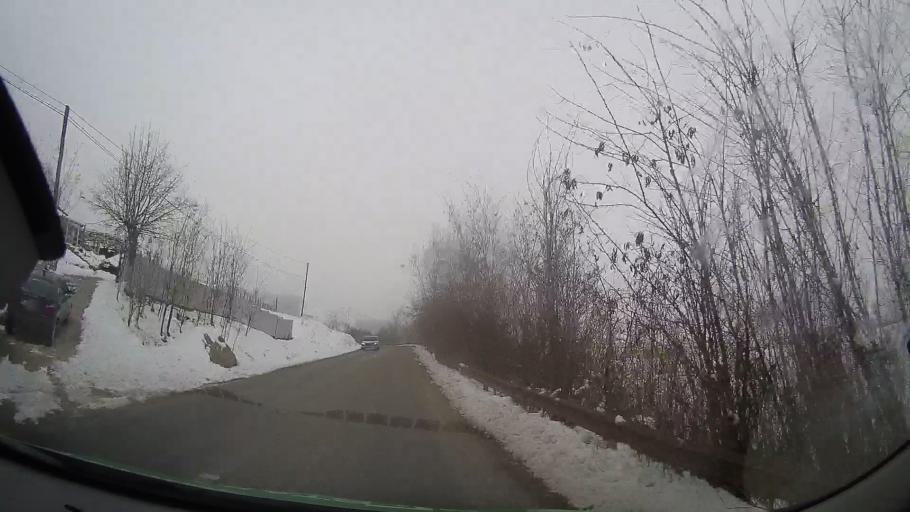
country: RO
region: Bacau
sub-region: Comuna Vultureni
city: Vultureni
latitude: 46.3947
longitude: 27.2777
